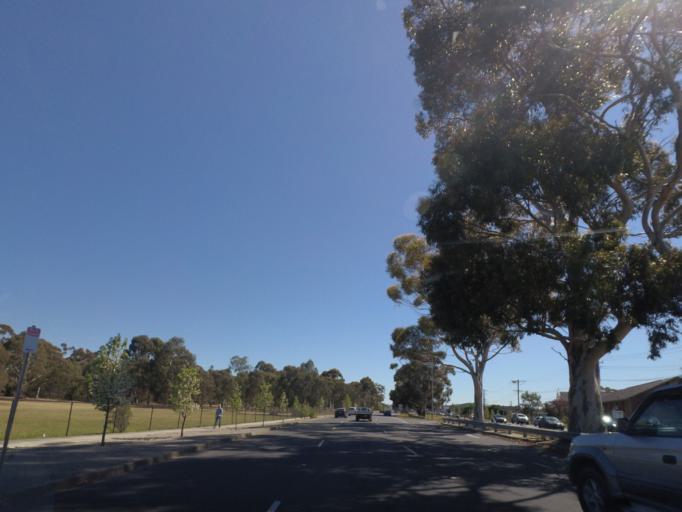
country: AU
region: Victoria
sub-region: Moreland
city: Fawkner
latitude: -37.7173
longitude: 144.9624
